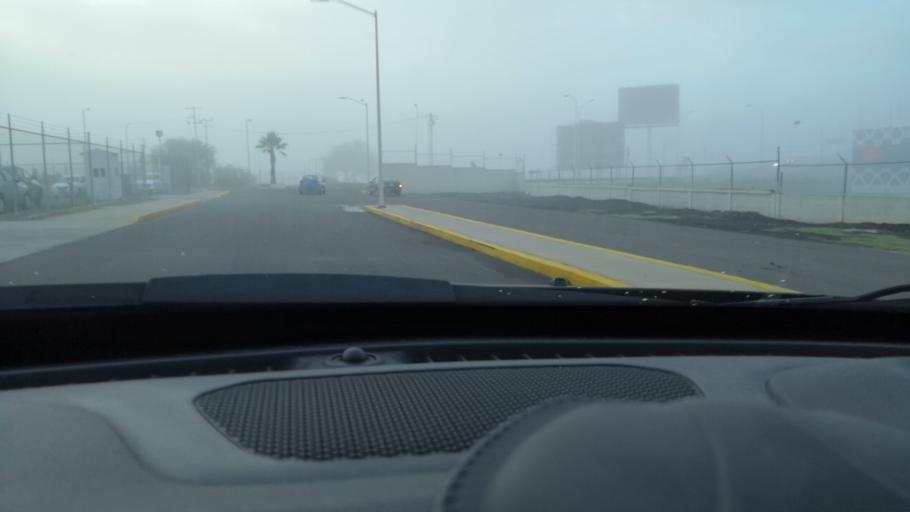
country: MX
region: Guanajuato
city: Colonia Nuevo Mexico
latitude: 20.9842
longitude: -101.4805
